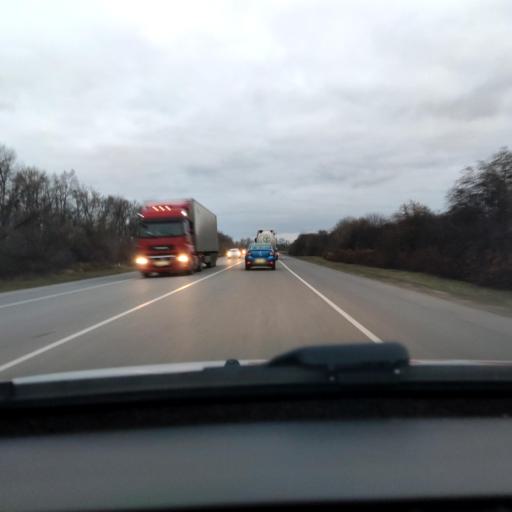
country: RU
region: Lipetsk
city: Borinskoye
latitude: 52.4512
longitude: 39.2963
